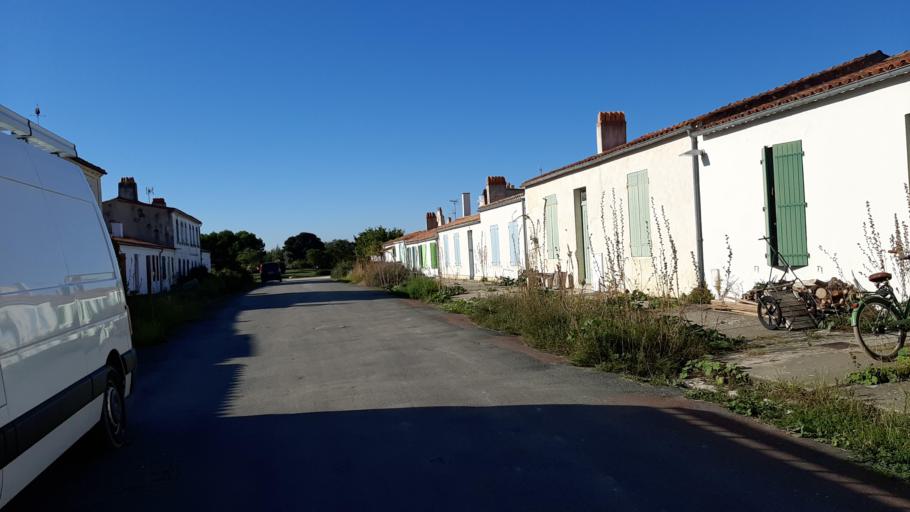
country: FR
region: Poitou-Charentes
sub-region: Departement de la Charente-Maritime
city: Boyard-Ville
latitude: 46.0122
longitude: -1.1749
